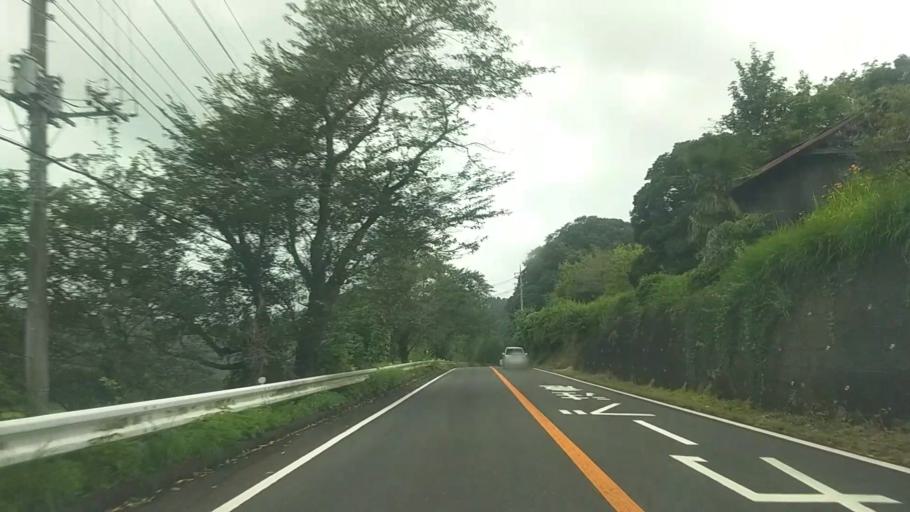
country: JP
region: Chiba
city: Kawaguchi
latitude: 35.2386
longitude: 140.0755
